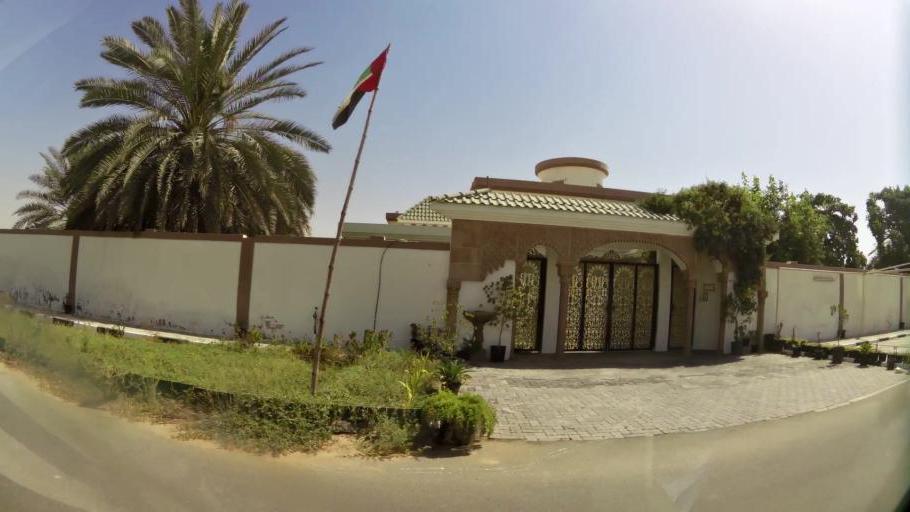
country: AE
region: Ajman
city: Ajman
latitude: 25.4071
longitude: 55.4747
